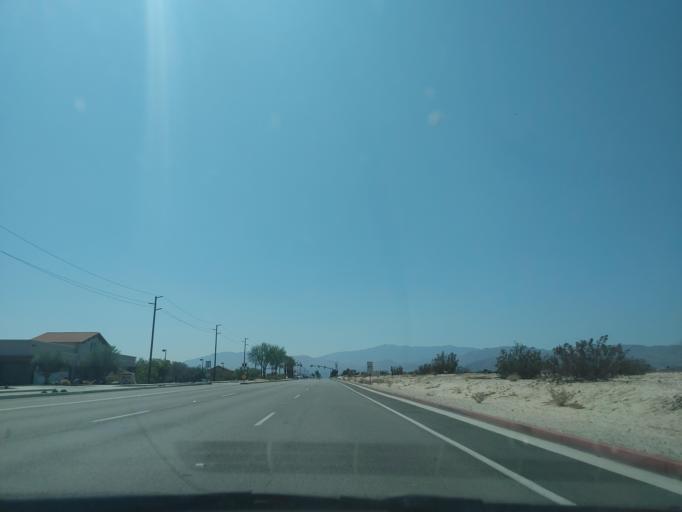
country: US
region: California
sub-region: Riverside County
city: Thousand Palms
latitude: 33.7972
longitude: -116.3883
